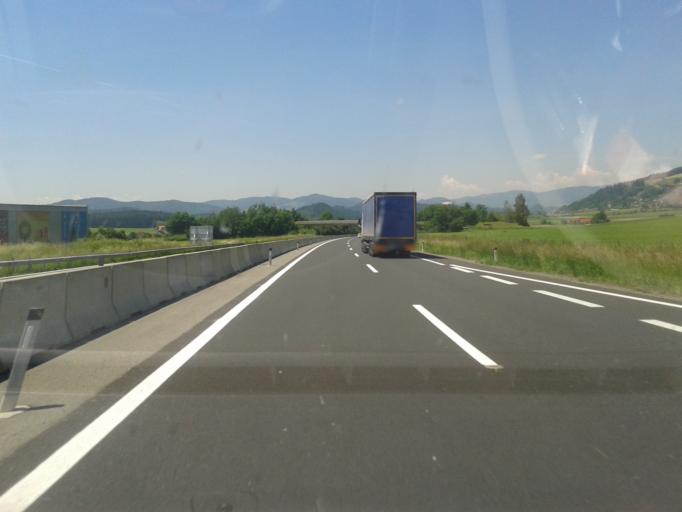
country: AT
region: Carinthia
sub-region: Politischer Bezirk Volkermarkt
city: Voelkermarkt
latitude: 46.6830
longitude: 14.6758
